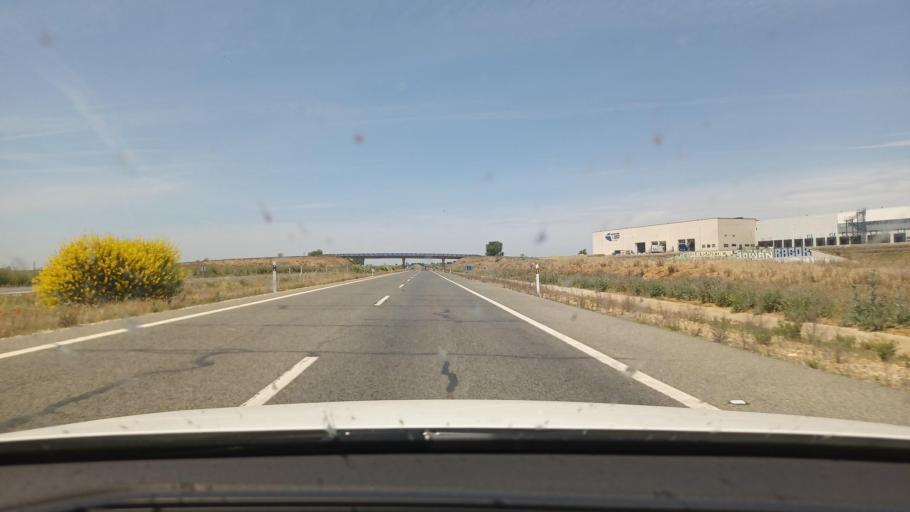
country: ES
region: Madrid
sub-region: Provincia de Madrid
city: Camarma de Esteruelas
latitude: 40.5243
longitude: -3.3874
